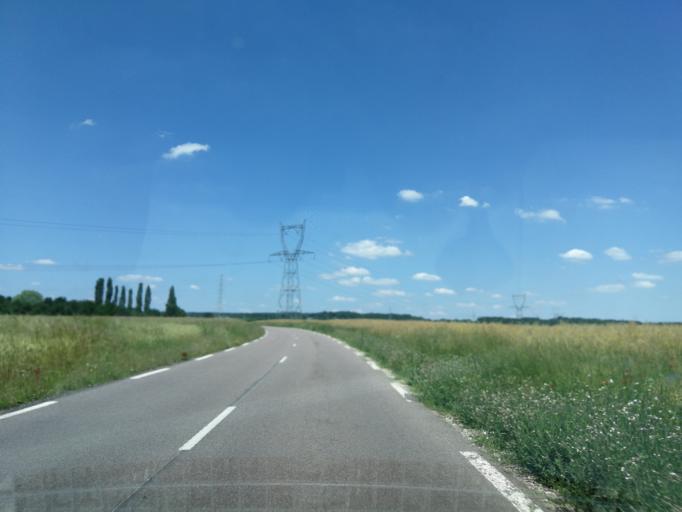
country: FR
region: Ile-de-France
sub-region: Departement de l'Essonne
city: Vaugrigneuse
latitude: 48.6099
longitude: 2.1264
